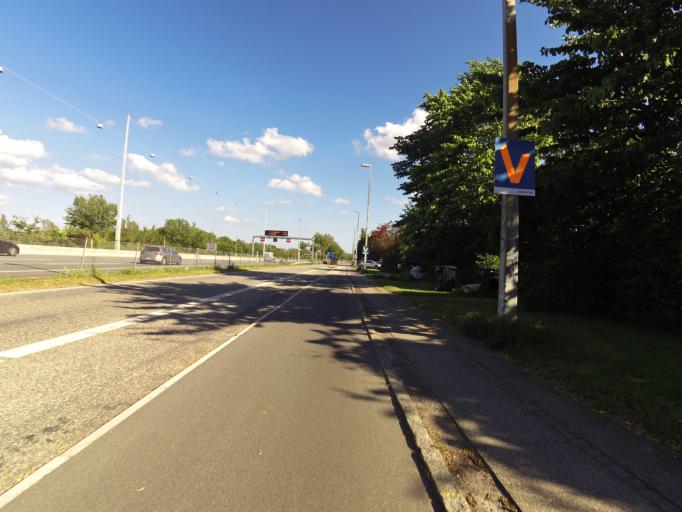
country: DK
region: Capital Region
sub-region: Lyngby-Tarbaek Kommune
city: Kongens Lyngby
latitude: 55.7471
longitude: 12.5292
